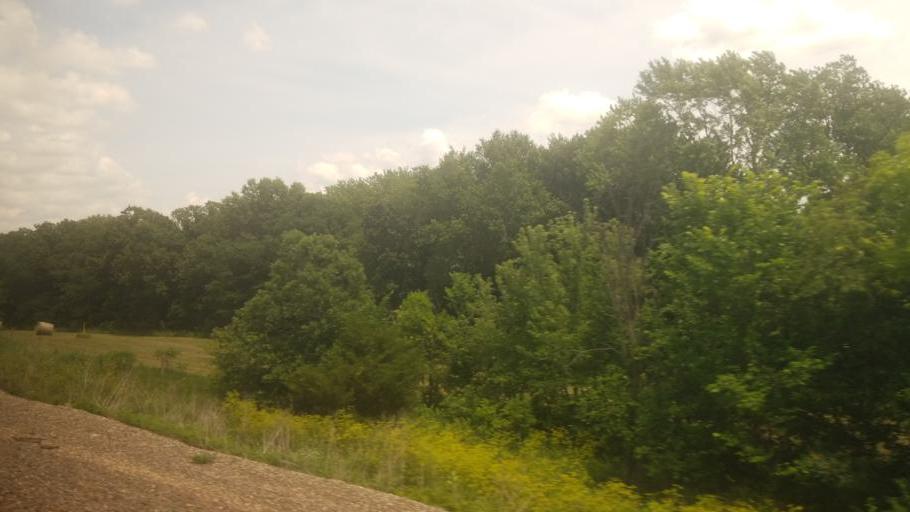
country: US
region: Missouri
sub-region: Macon County
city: La Plata
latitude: 40.0522
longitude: -92.4670
